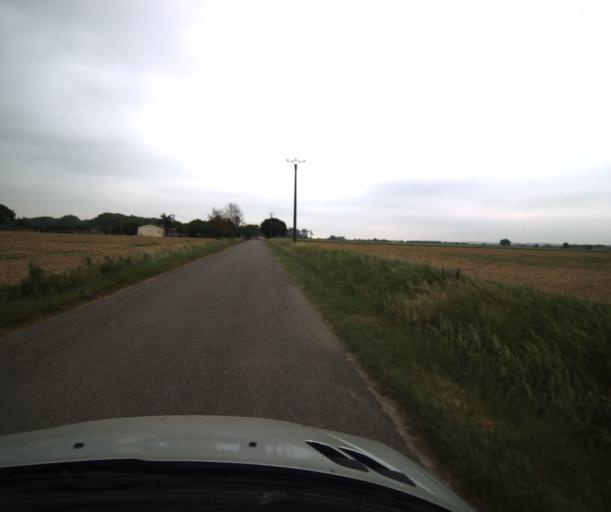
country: FR
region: Midi-Pyrenees
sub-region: Departement du Tarn-et-Garonne
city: Saint-Nicolas-de-la-Grave
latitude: 44.0484
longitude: 1.0227
